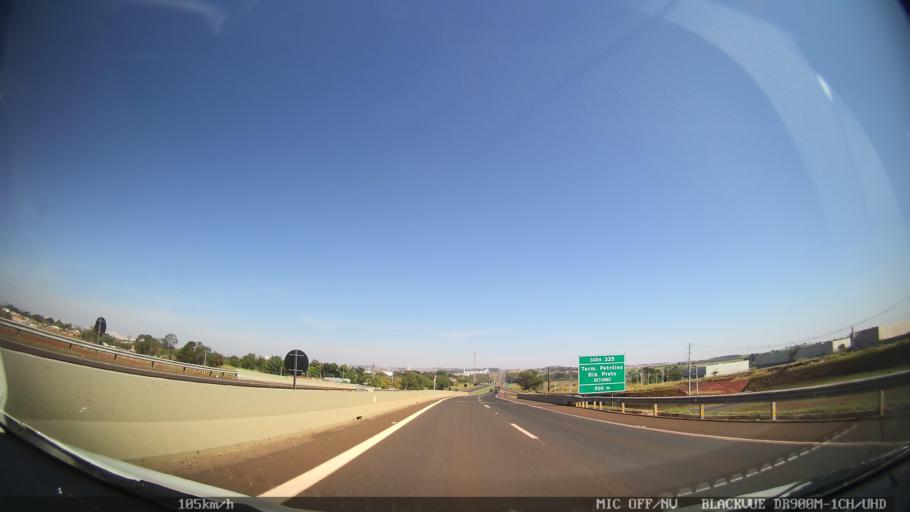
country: BR
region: Sao Paulo
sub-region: Ribeirao Preto
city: Ribeirao Preto
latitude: -21.1011
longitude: -47.8006
